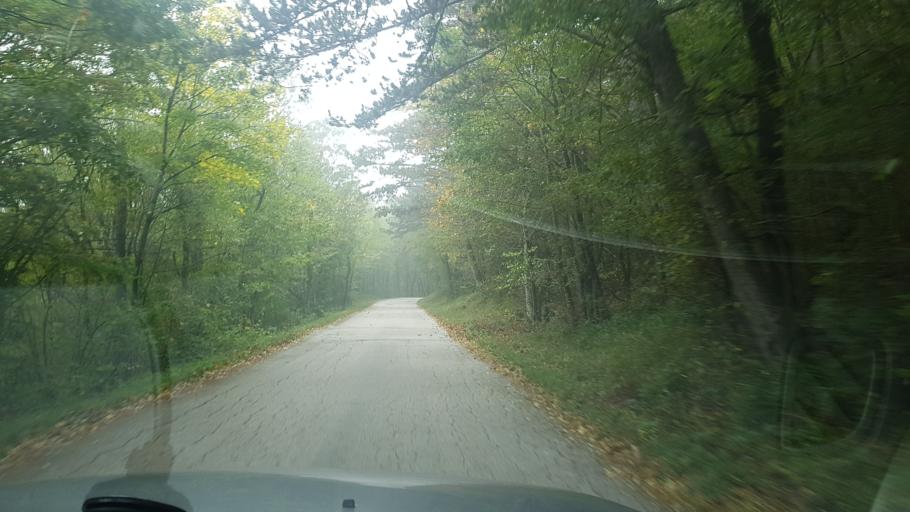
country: HR
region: Istarska
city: Buzet
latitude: 45.4515
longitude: 14.0243
